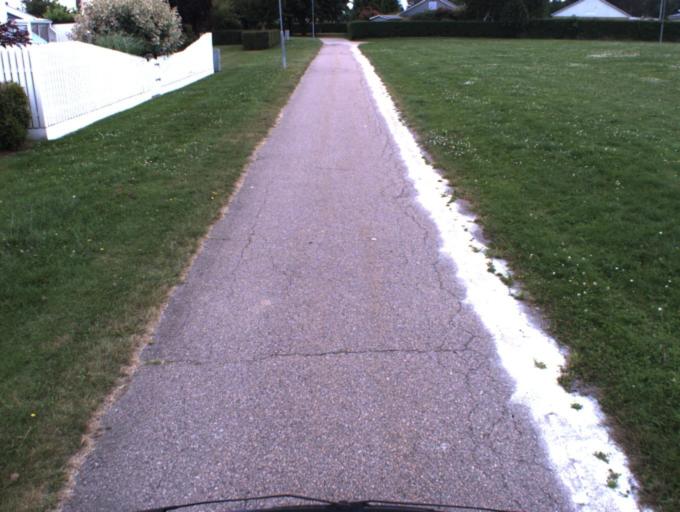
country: SE
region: Skane
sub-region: Helsingborg
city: Rydeback
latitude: 55.9691
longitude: 12.7636
